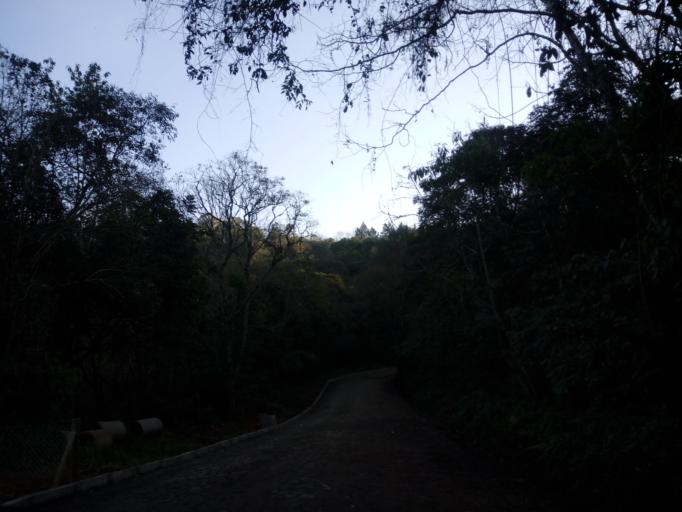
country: BR
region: Santa Catarina
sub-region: Chapeco
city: Chapeco
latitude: -27.2326
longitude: -52.6810
